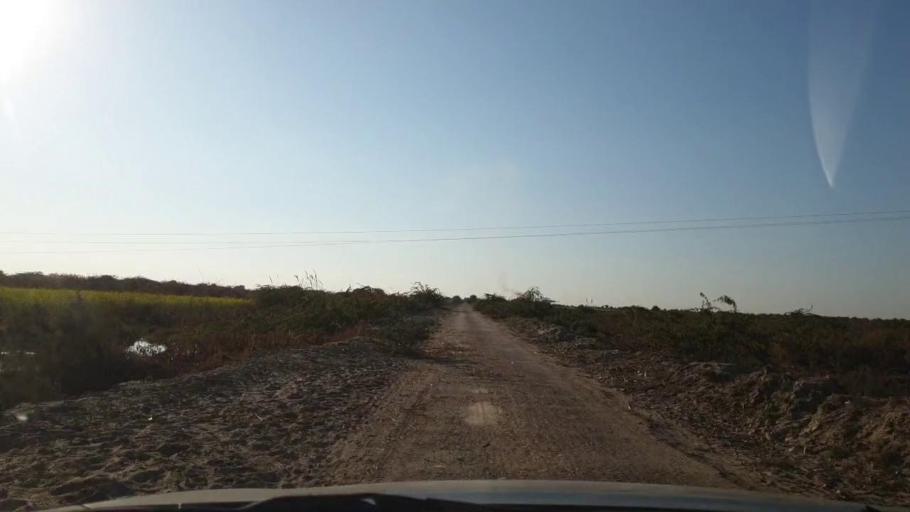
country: PK
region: Sindh
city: Jhol
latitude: 25.8980
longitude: 68.9370
